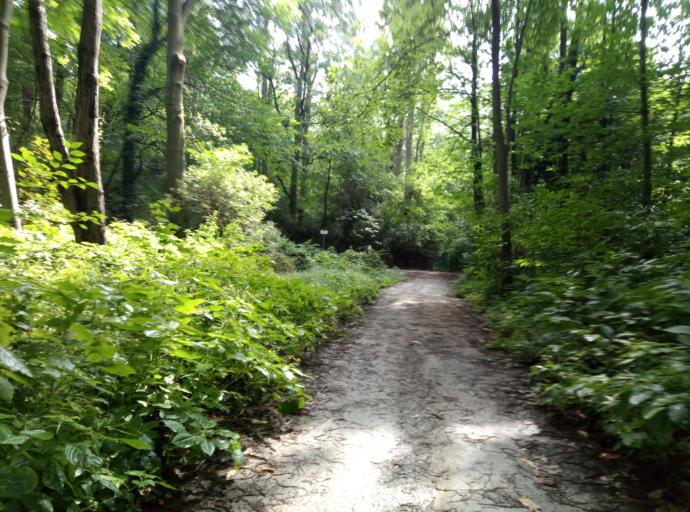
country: BE
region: Flanders
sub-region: Provincie Vlaams-Brabant
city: Holsbeek
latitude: 50.9076
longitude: 4.7285
